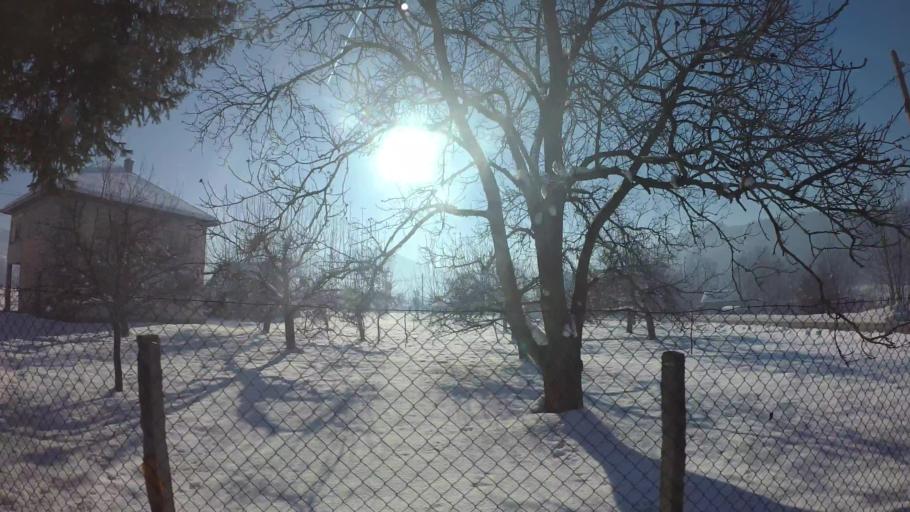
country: BA
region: Federation of Bosnia and Herzegovina
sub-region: Kanton Sarajevo
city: Sarajevo
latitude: 43.8170
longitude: 18.3833
